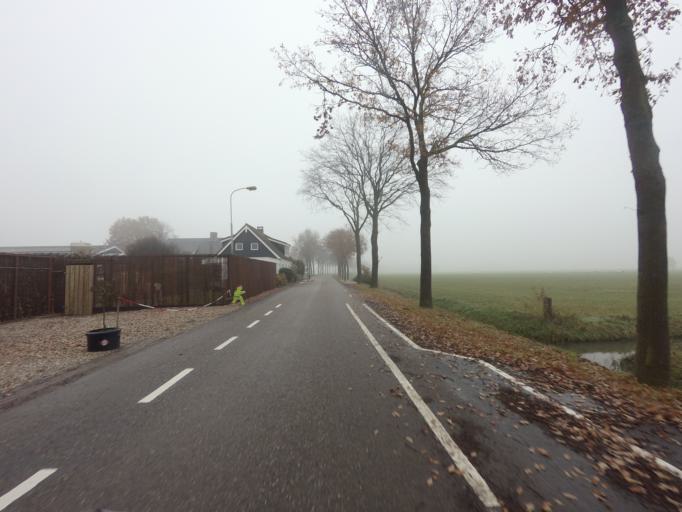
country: NL
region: Gelderland
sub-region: Gemeente Zaltbommel
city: Nederhemert-Noord
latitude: 51.7734
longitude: 5.1982
